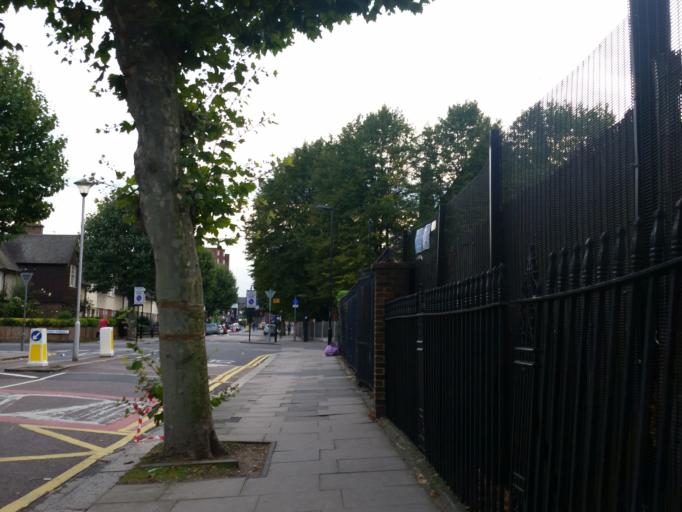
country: GB
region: England
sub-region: Greater London
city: Harringay
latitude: 51.5951
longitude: -0.1033
